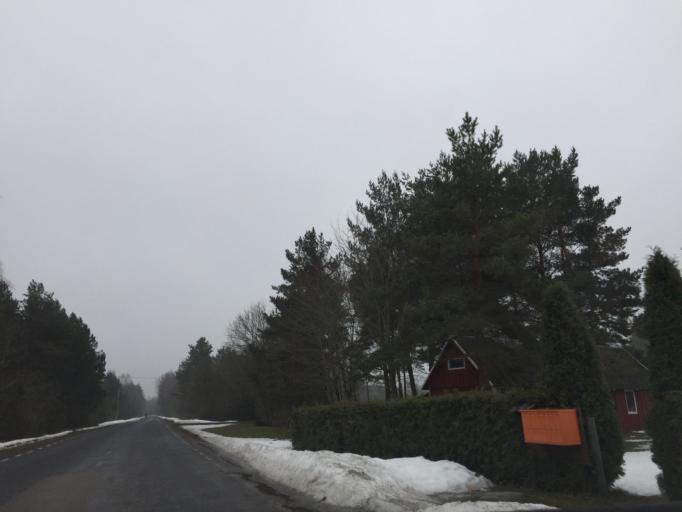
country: EE
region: Saare
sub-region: Kuressaare linn
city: Kuressaare
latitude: 58.2695
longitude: 22.5863
